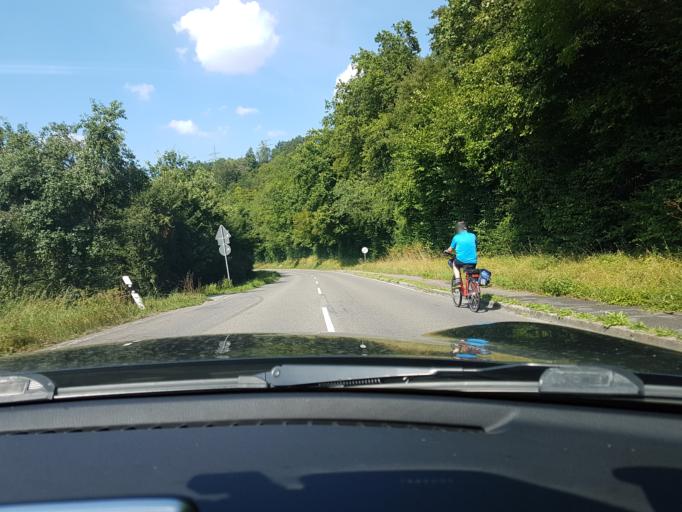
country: DE
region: Baden-Wuerttemberg
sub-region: Regierungsbezirk Stuttgart
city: Mockmuhl
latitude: 49.3294
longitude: 9.3535
